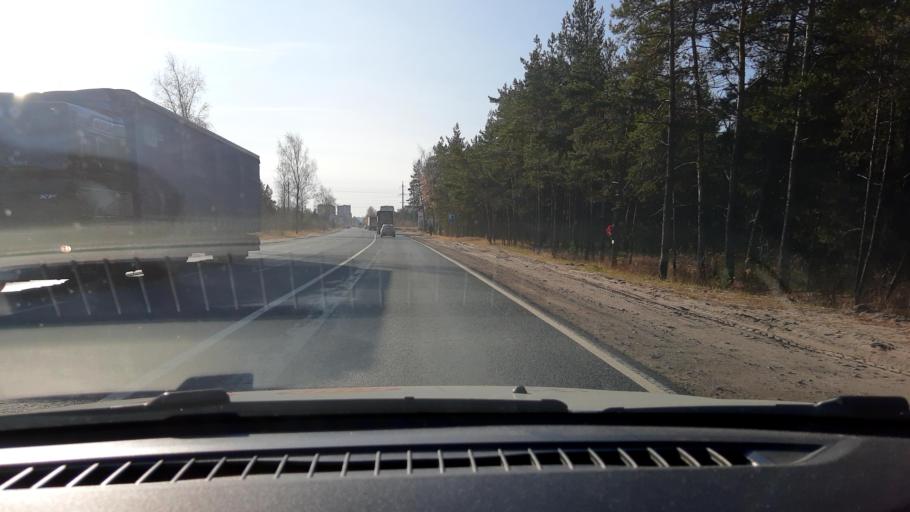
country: RU
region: Nizjnij Novgorod
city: Dzerzhinsk
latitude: 56.2642
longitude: 43.4694
